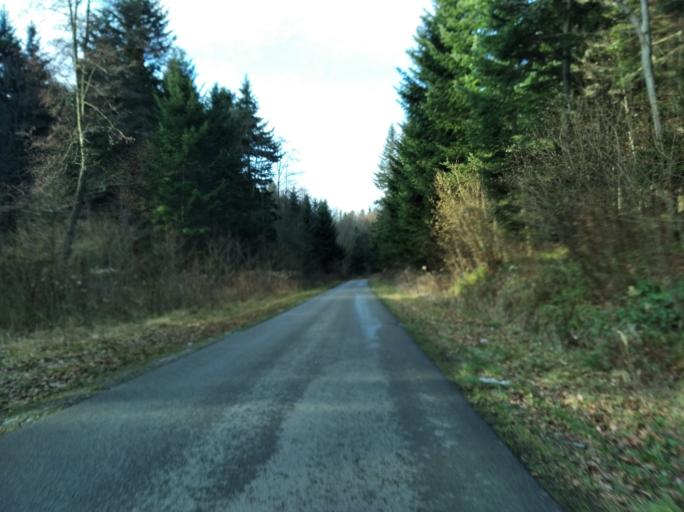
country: PL
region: Subcarpathian Voivodeship
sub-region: Powiat strzyzowski
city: Konieczkowa
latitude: 49.8257
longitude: 21.9440
